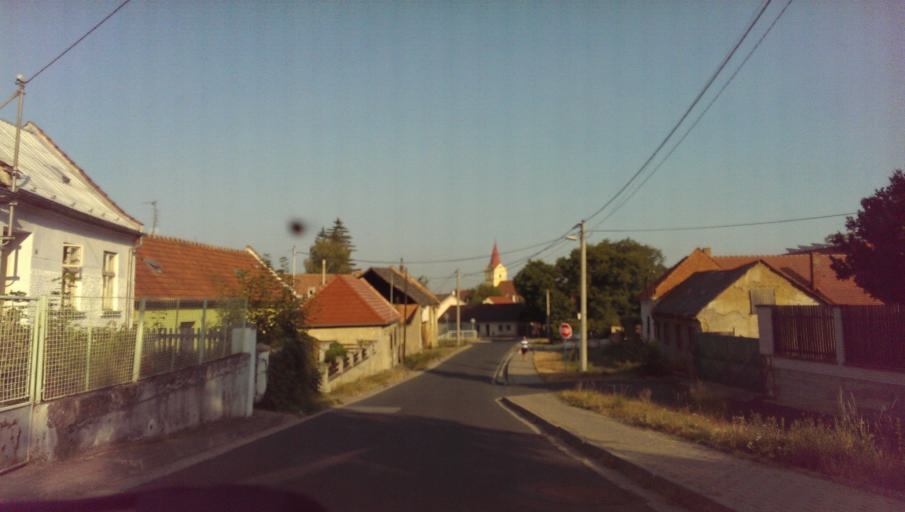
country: CZ
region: Zlin
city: Korycany
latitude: 49.1042
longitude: 17.1666
